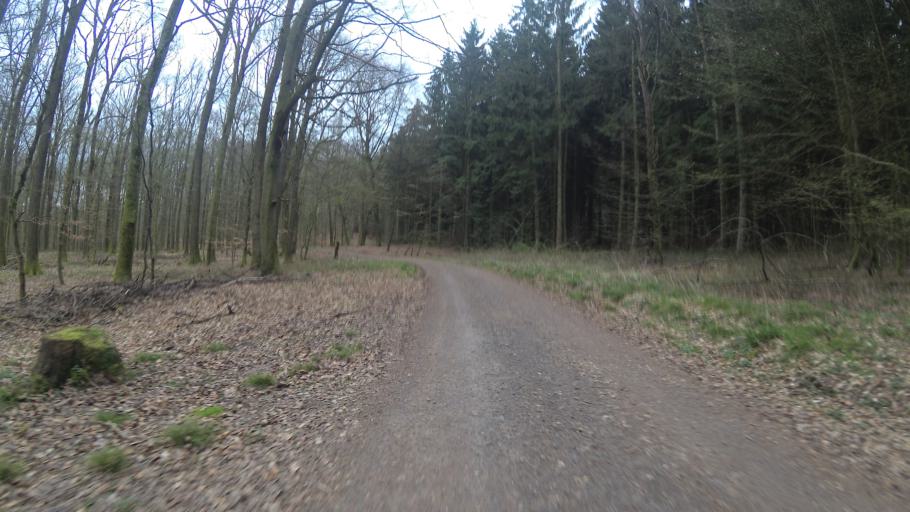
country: DE
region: Saarland
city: Hangard
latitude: 49.4336
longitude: 7.2116
